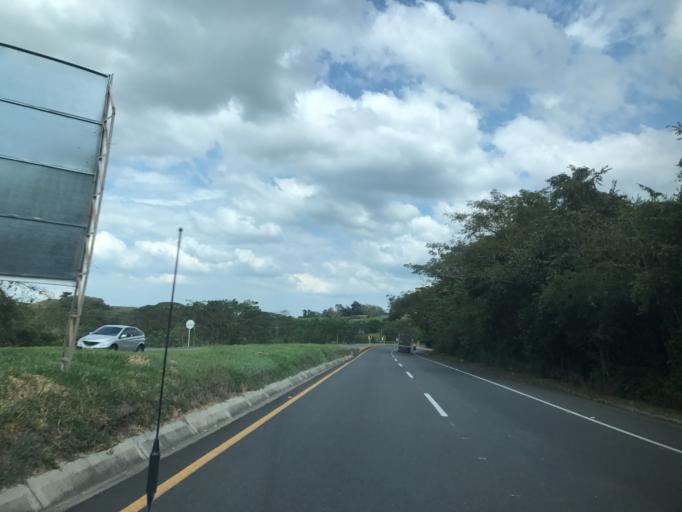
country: CO
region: Valle del Cauca
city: Obando
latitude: 4.6147
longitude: -75.9511
